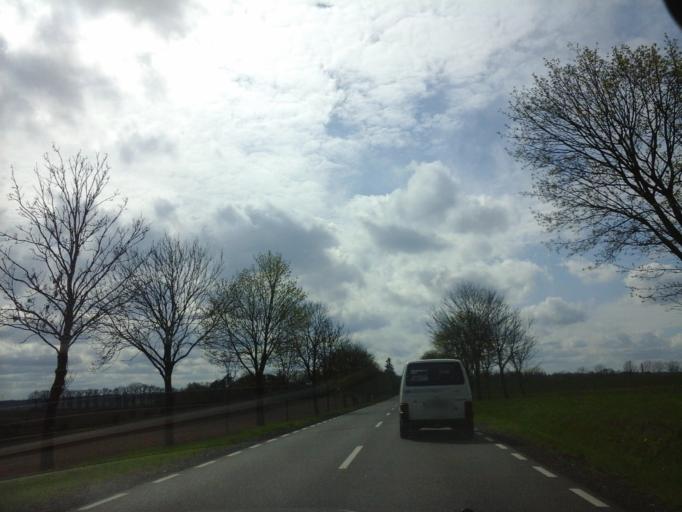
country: PL
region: West Pomeranian Voivodeship
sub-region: Powiat choszczenski
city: Pelczyce
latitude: 53.0936
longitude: 15.3154
